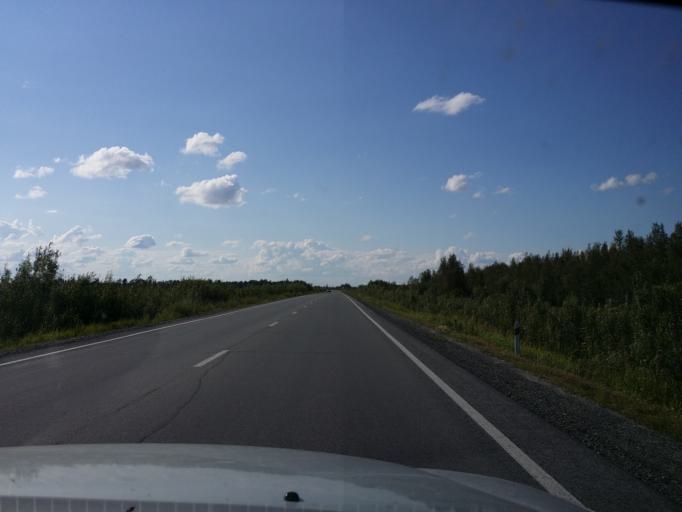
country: RU
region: Khanty-Mansiyskiy Avtonomnyy Okrug
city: Lokosovo
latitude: 61.4387
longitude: 74.7785
